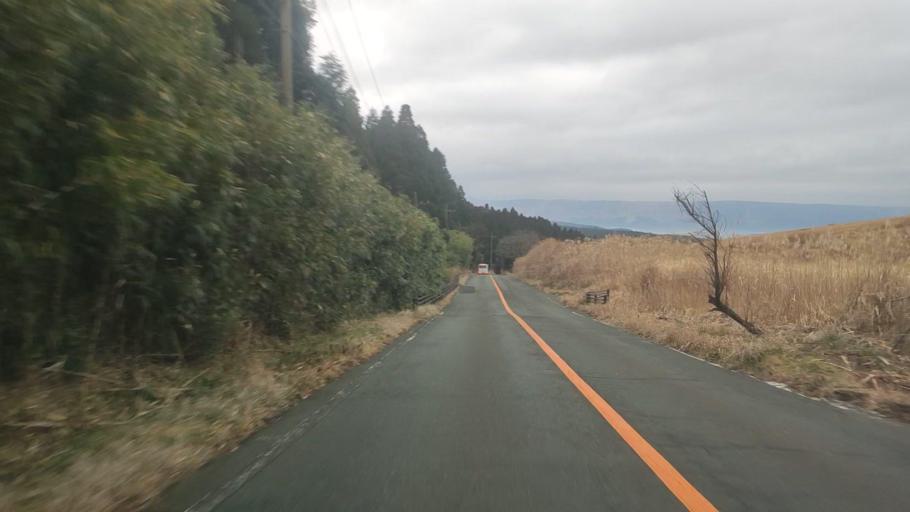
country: JP
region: Kumamoto
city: Aso
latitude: 32.9094
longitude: 131.1365
